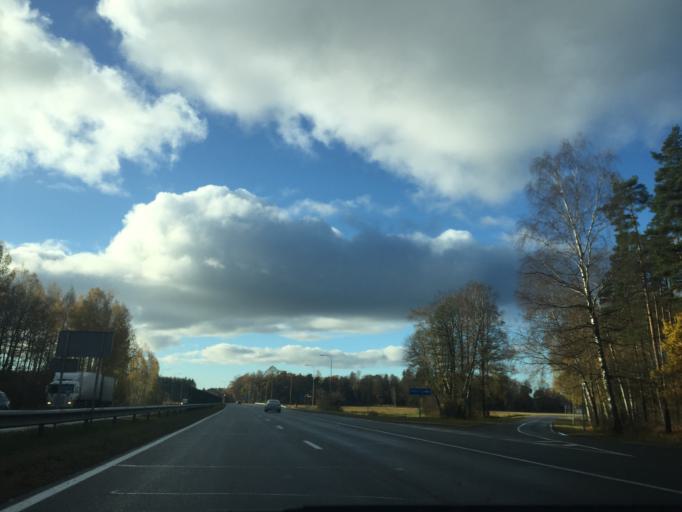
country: LV
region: Babite
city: Pinki
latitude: 56.9474
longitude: 23.9241
